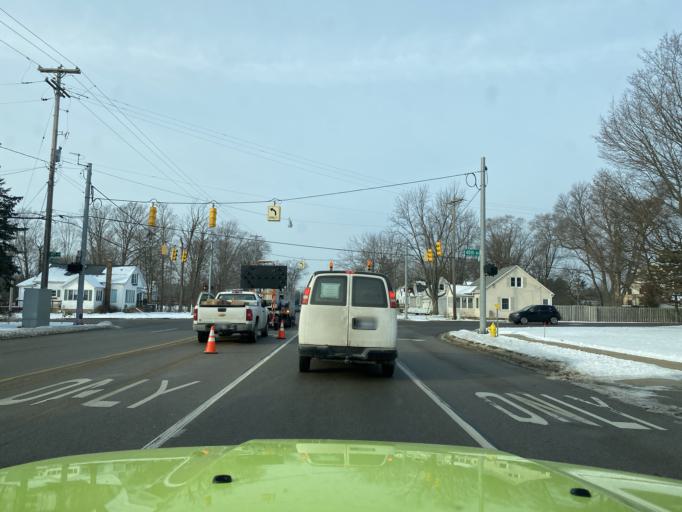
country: US
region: Michigan
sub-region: Ottawa County
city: Hudsonville
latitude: 42.8854
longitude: -85.8811
